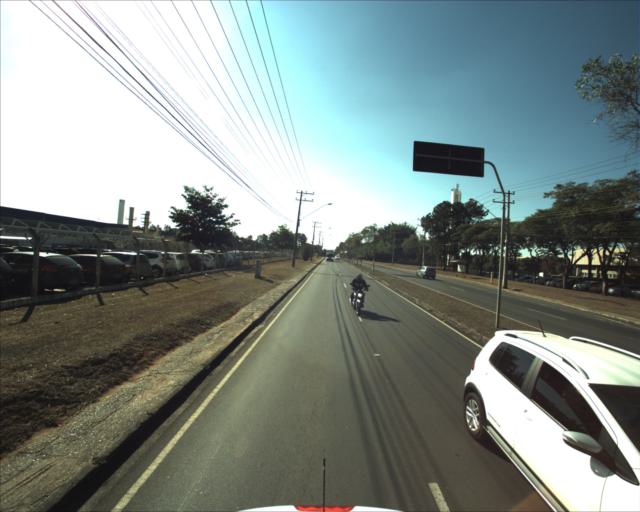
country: BR
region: Sao Paulo
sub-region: Sorocaba
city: Sorocaba
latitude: -23.4384
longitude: -47.4164
